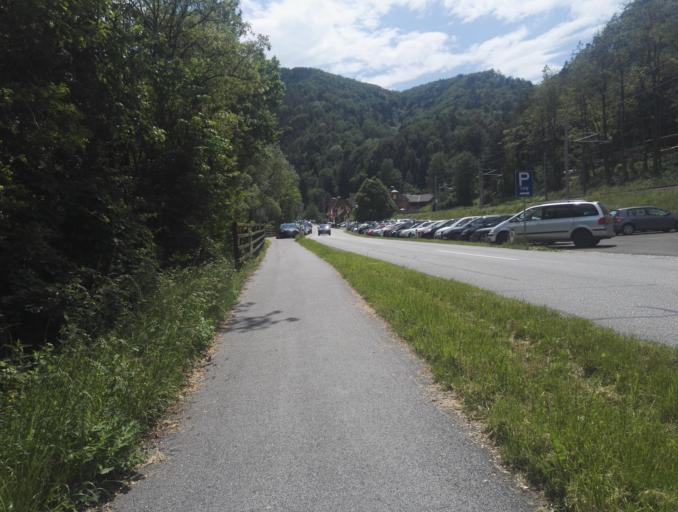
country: AT
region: Styria
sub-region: Politischer Bezirk Graz-Umgebung
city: Deutschfeistritz
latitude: 47.1608
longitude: 15.3167
